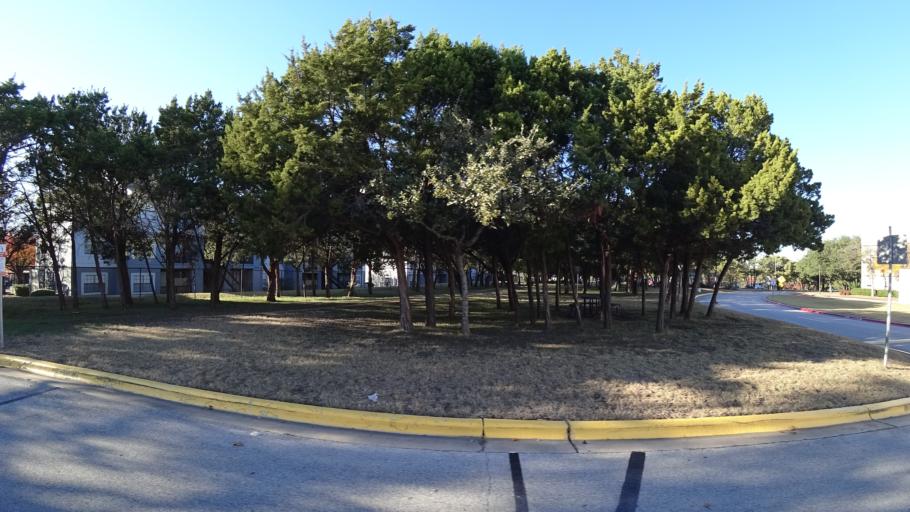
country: US
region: Texas
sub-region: Travis County
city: Wells Branch
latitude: 30.4032
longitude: -97.7056
